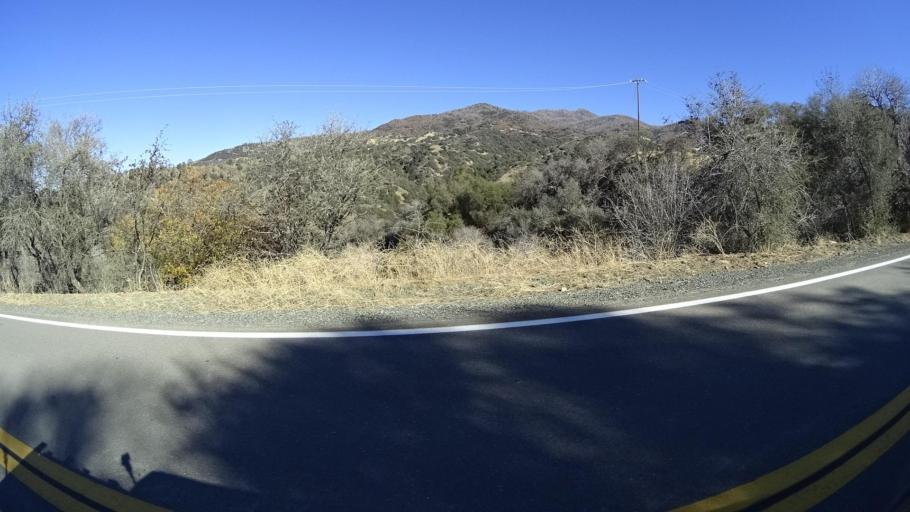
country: US
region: California
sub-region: Kern County
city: Alta Sierra
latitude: 35.7379
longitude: -118.6430
